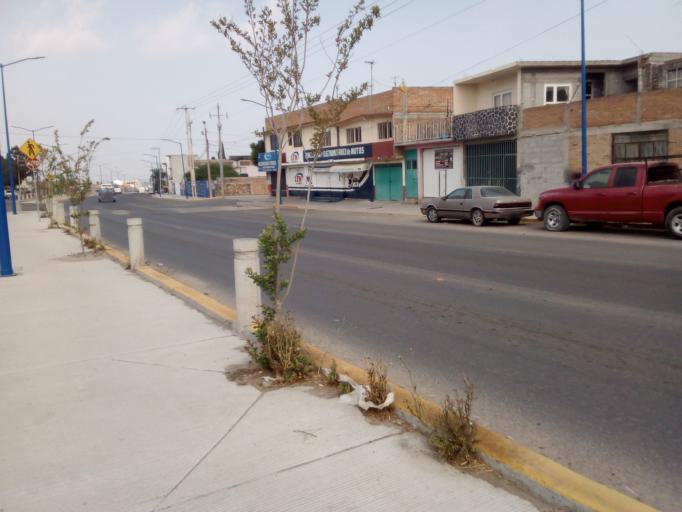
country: MX
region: Guerrero
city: San Luis de la Paz
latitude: 21.2879
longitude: -100.5193
